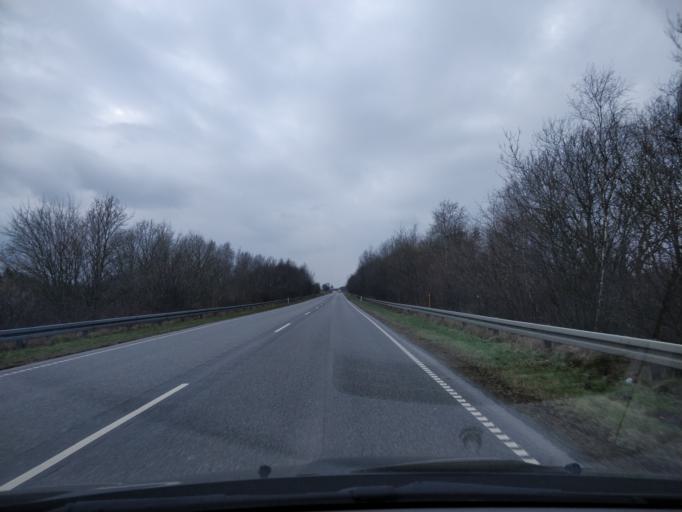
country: DK
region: South Denmark
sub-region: Vejle Kommune
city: Brejning
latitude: 55.6263
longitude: 9.7230
